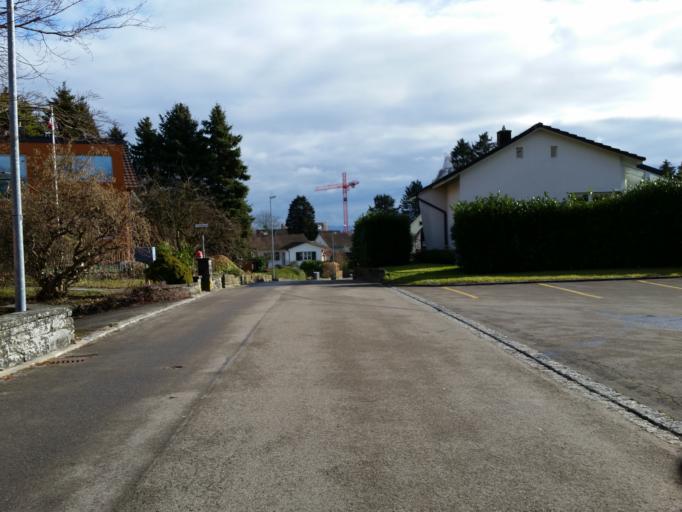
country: CH
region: Thurgau
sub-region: Arbon District
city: Salmsach
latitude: 47.5551
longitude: 9.3665
